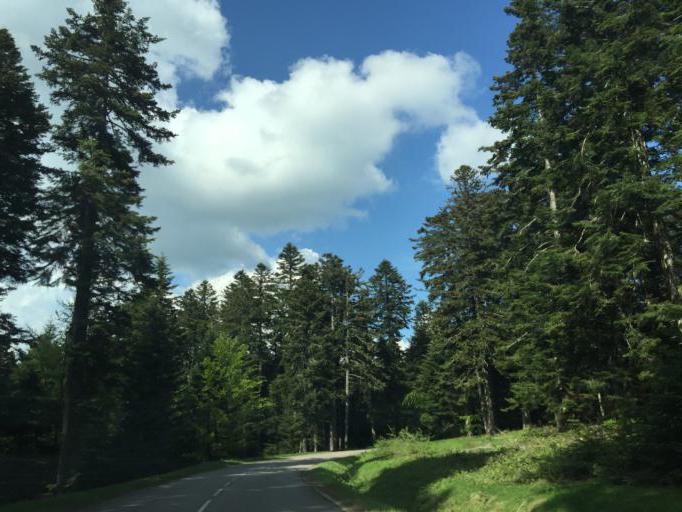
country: FR
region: Rhone-Alpes
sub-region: Departement de la Loire
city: Saint-Genest-Malifaux
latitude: 45.3231
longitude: 4.4723
